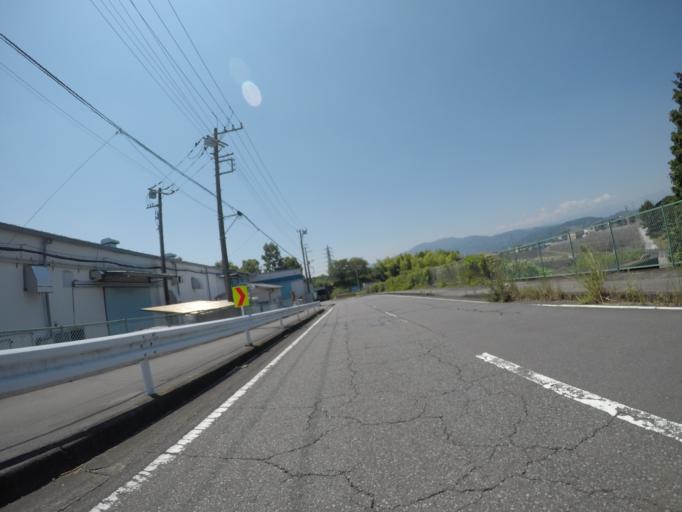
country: JP
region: Shizuoka
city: Fuji
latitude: 35.1806
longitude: 138.6704
